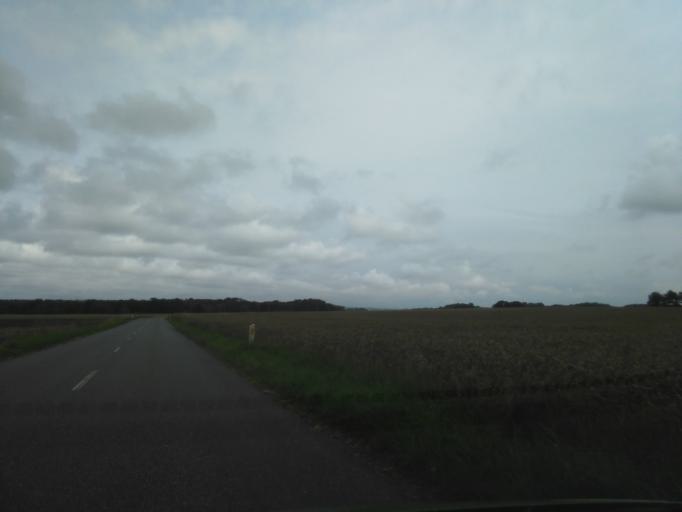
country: DK
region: Central Jutland
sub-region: Odder Kommune
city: Odder
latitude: 55.9560
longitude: 10.1118
